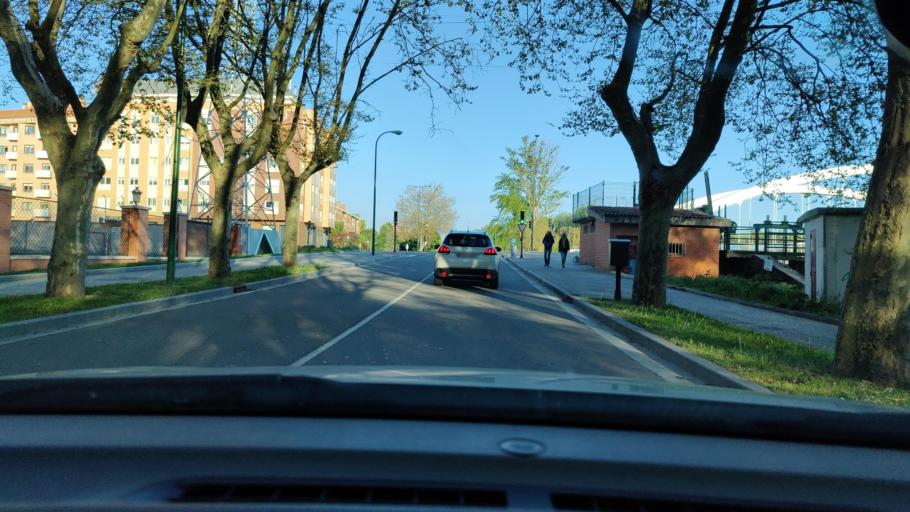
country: ES
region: Castille and Leon
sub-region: Provincia de Burgos
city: Villagonzalo-Pedernales
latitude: 42.3453
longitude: -3.7278
